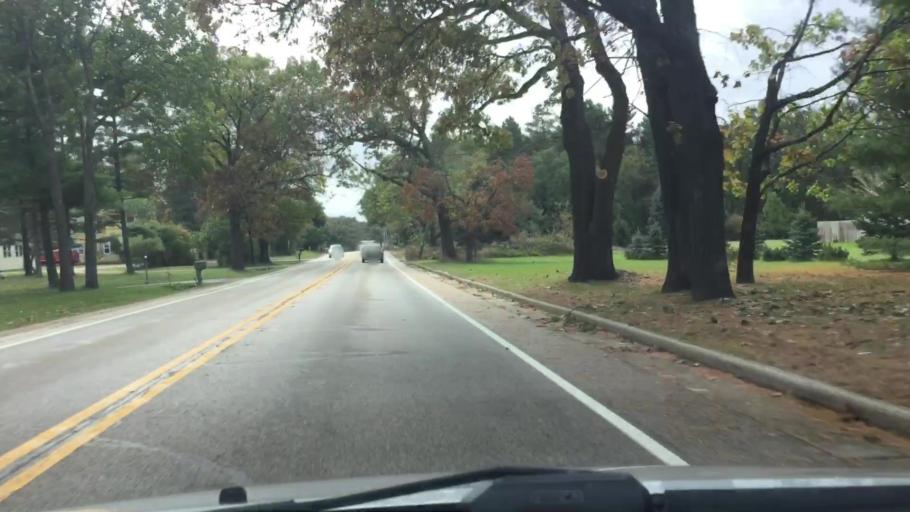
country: US
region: Wisconsin
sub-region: Waukesha County
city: Dousman
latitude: 42.9942
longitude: -88.4634
